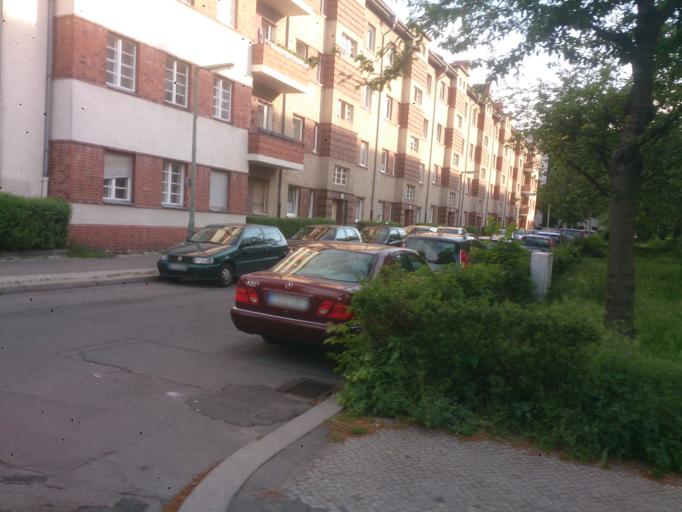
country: DE
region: Berlin
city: Treptow Bezirk
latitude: 52.4815
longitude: 13.4506
